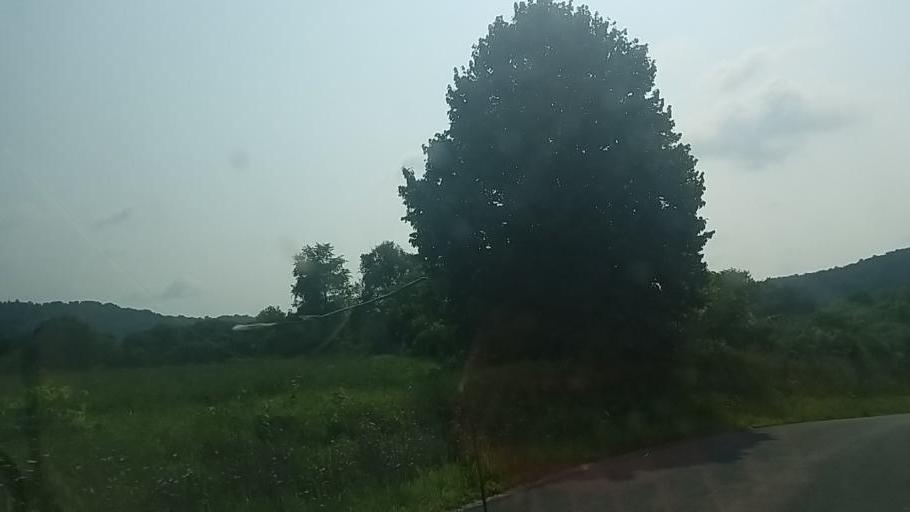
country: US
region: New York
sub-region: Montgomery County
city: Fonda
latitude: 42.9720
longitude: -74.4306
